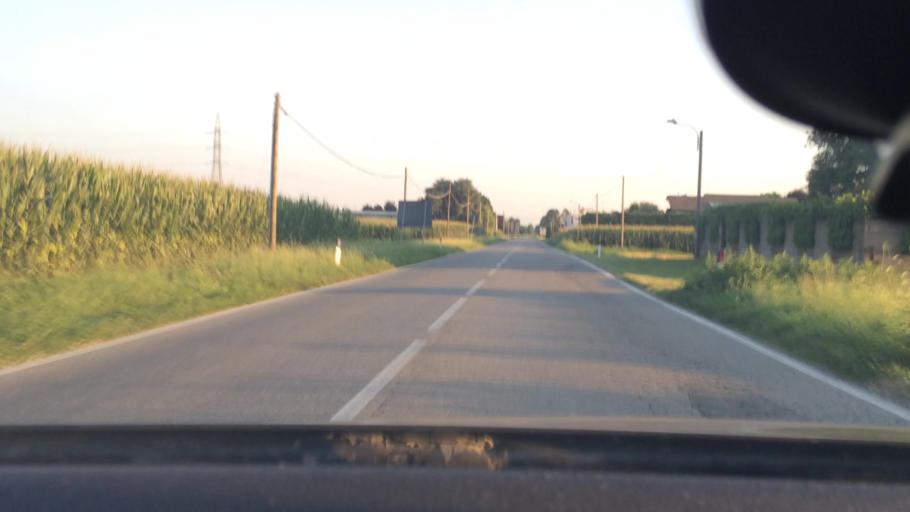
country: IT
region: Lombardy
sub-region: Provincia di Como
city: Turate
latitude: 45.6706
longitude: 9.0021
